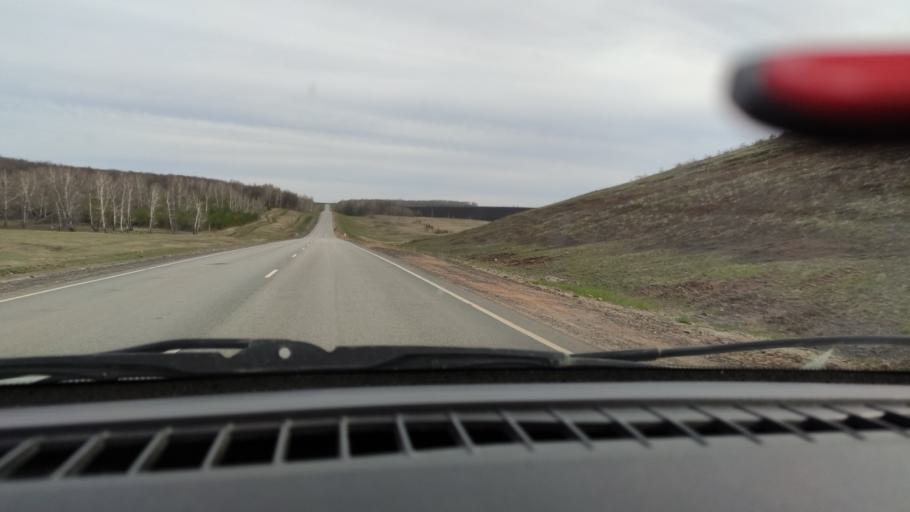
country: RU
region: Bashkortostan
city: Yermolayevo
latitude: 52.6921
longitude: 55.8567
